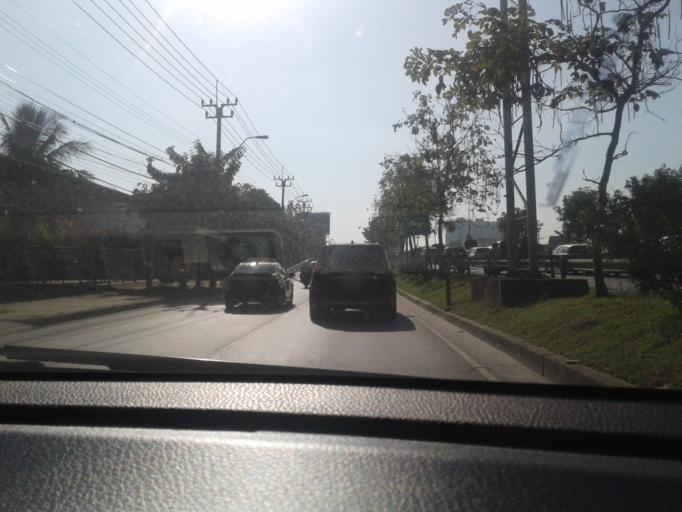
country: TH
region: Bangkok
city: Phasi Charoen
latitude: 13.7297
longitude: 100.4525
